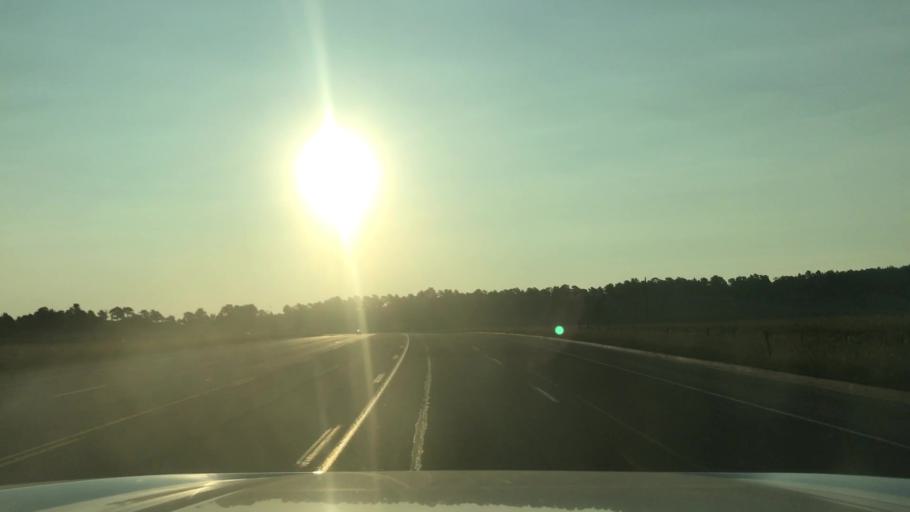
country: US
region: Wyoming
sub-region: Natrona County
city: Evansville
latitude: 42.8396
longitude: -106.2215
